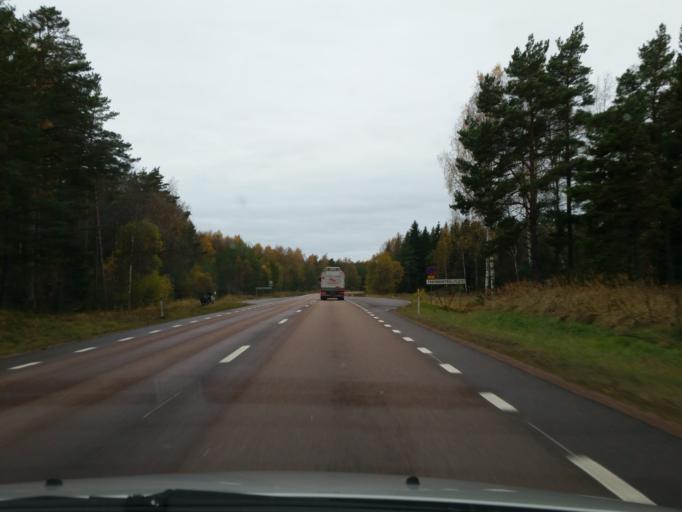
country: AX
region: Alands landsbygd
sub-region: Lemland
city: Lemland
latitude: 60.0642
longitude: 20.0567
